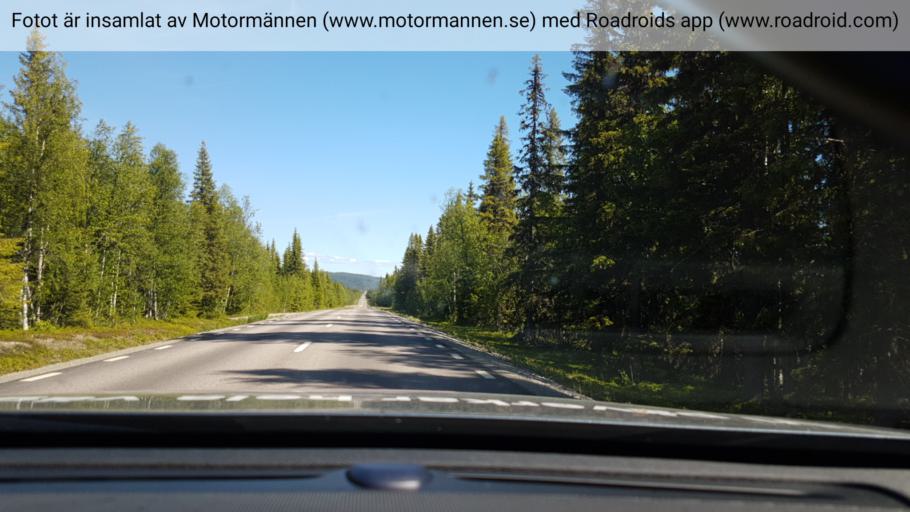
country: SE
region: Vaesterbotten
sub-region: Asele Kommun
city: Insjon
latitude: 64.7282
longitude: 17.5534
